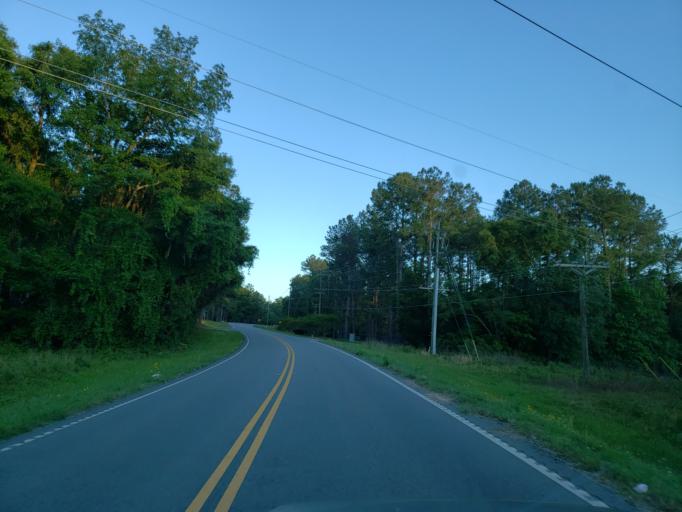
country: US
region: Georgia
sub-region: Lowndes County
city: Valdosta
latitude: 30.6843
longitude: -83.2387
